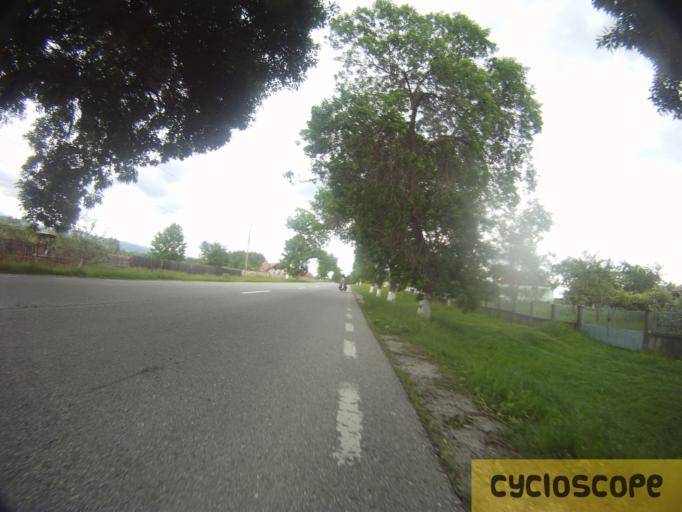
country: RO
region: Gorj
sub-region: Comuna Baia de Fier
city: Baia de Fier
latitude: 45.1391
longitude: 23.7442
